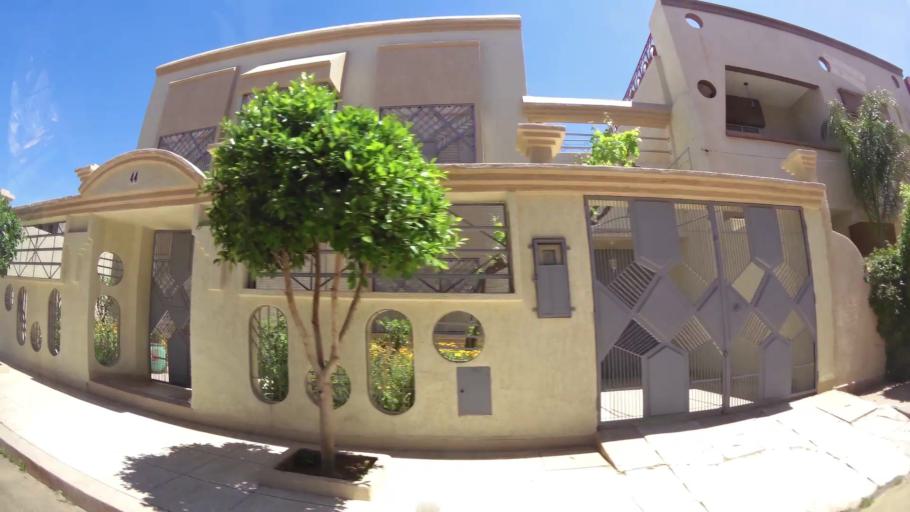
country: MA
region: Oriental
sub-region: Oujda-Angad
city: Oujda
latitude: 34.6629
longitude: -1.9449
